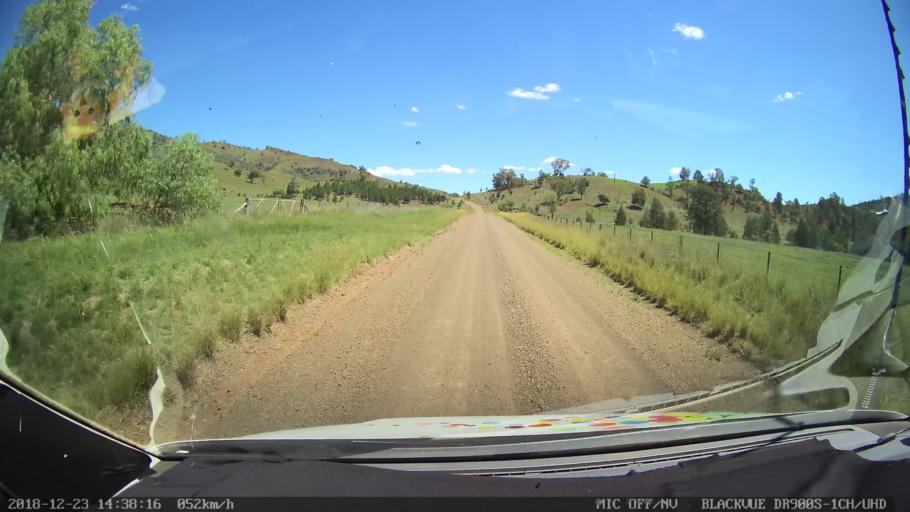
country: AU
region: New South Wales
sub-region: Tamworth Municipality
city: Manilla
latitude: -30.6201
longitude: 150.9059
